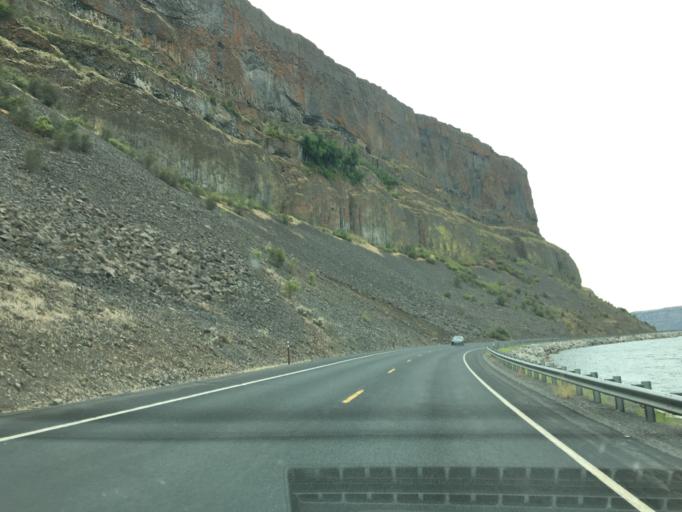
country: US
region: Washington
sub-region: Okanogan County
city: Coulee Dam
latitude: 47.8108
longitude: -119.1630
